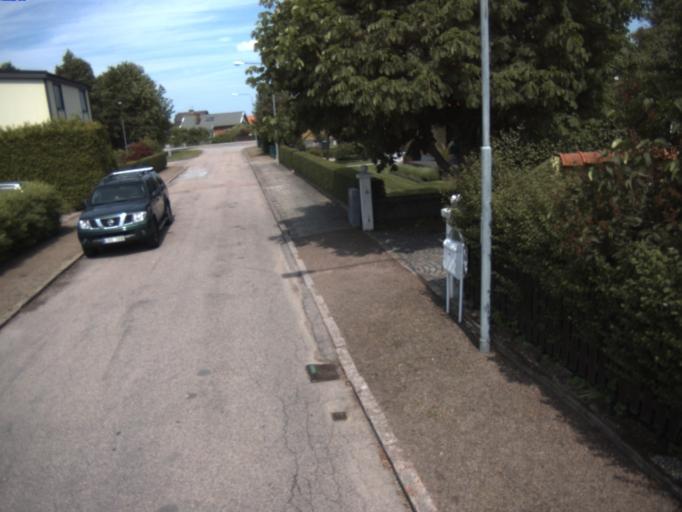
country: SE
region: Skane
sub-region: Helsingborg
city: Helsingborg
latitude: 56.0434
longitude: 12.7257
